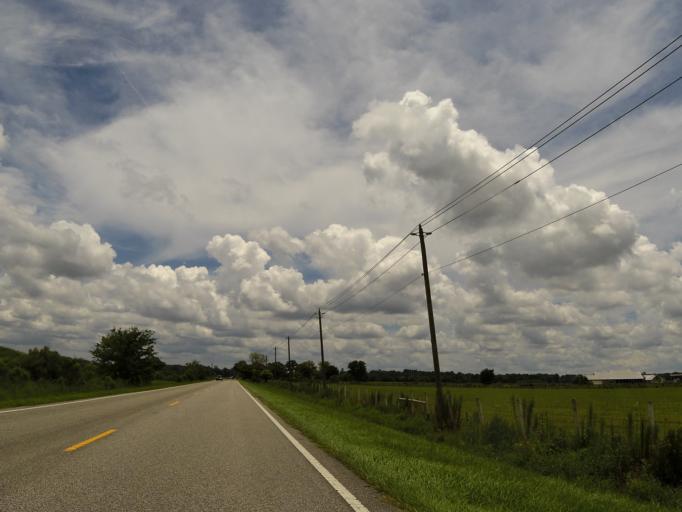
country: US
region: Florida
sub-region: Putnam County
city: East Palatka
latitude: 29.6886
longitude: -81.4800
